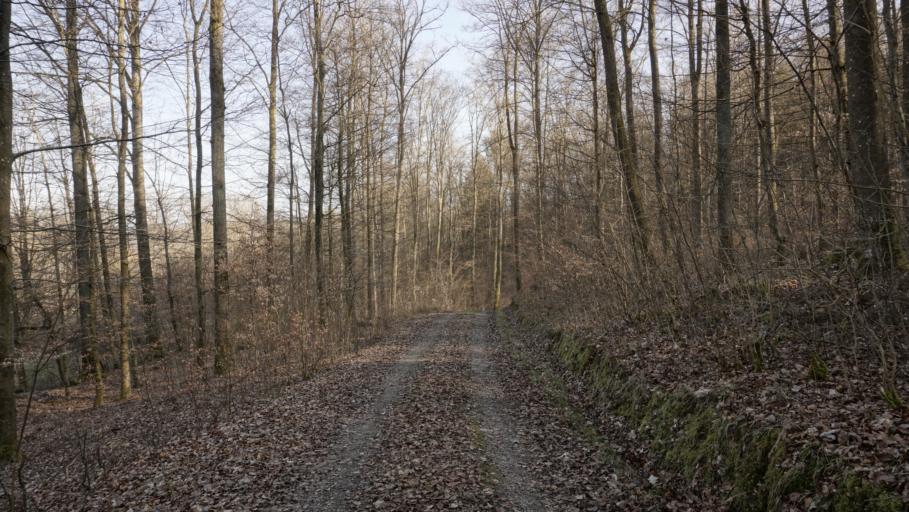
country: DE
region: Baden-Wuerttemberg
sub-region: Karlsruhe Region
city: Mosbach
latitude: 49.3767
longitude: 9.1418
